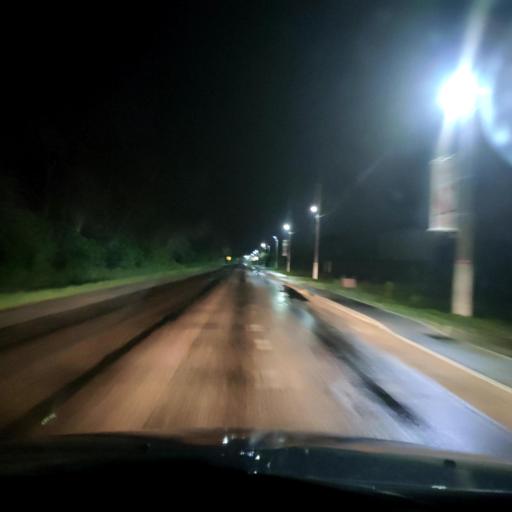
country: RU
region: Voronezj
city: Novaya Usman'
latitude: 51.6384
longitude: 39.3322
